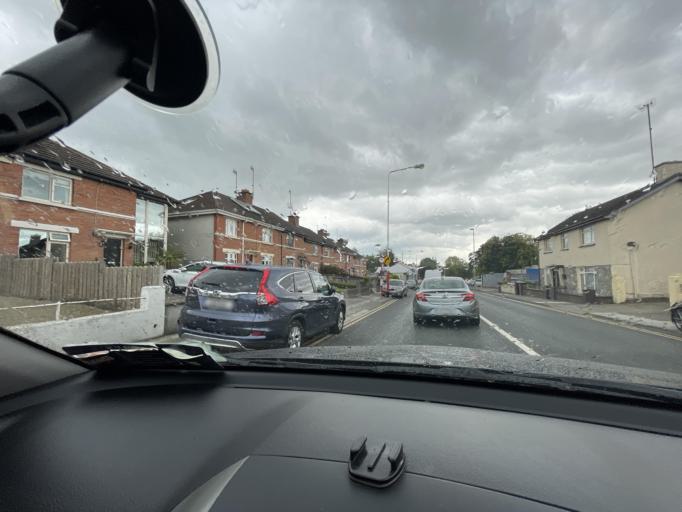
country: IE
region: Leinster
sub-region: Lu
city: Drogheda
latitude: 53.7205
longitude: -6.3577
